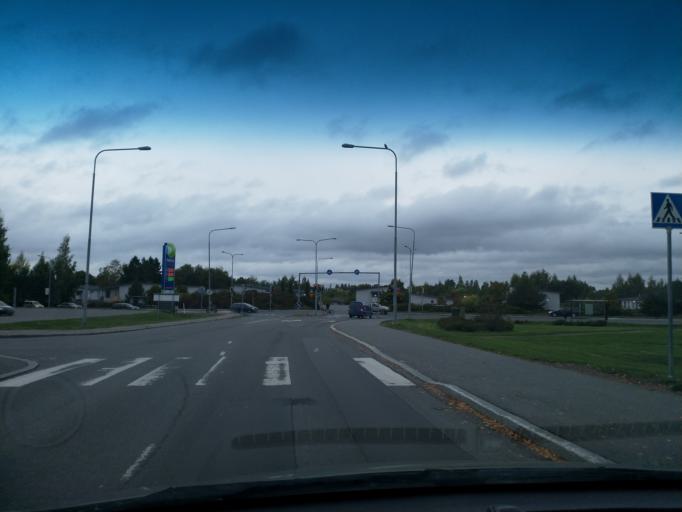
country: FI
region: Pirkanmaa
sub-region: Tampere
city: Tampere
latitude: 61.4777
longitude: 23.8415
